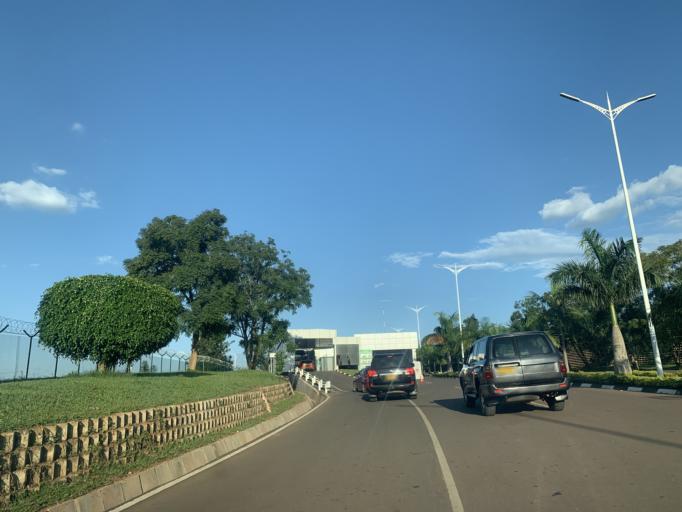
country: RW
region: Kigali
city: Kigali
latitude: -1.9638
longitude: 30.1306
